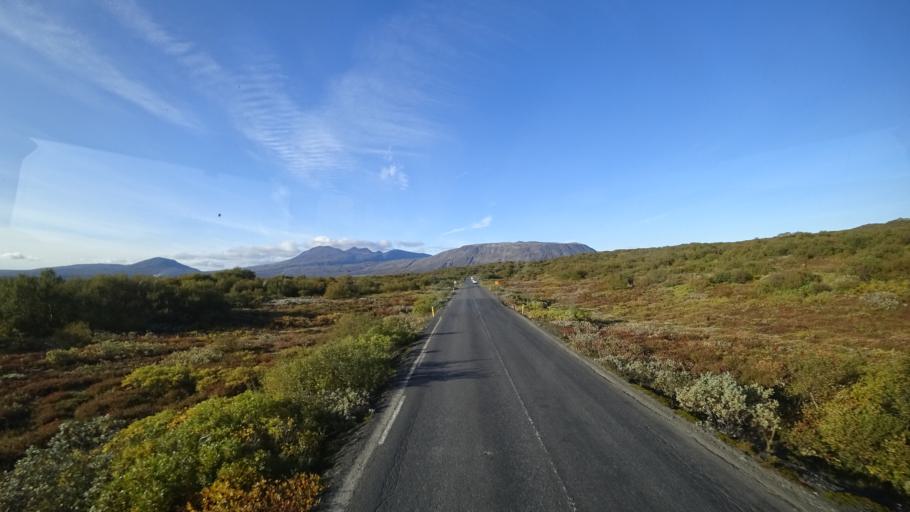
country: IS
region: South
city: Hveragerdi
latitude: 64.2550
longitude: -21.0275
